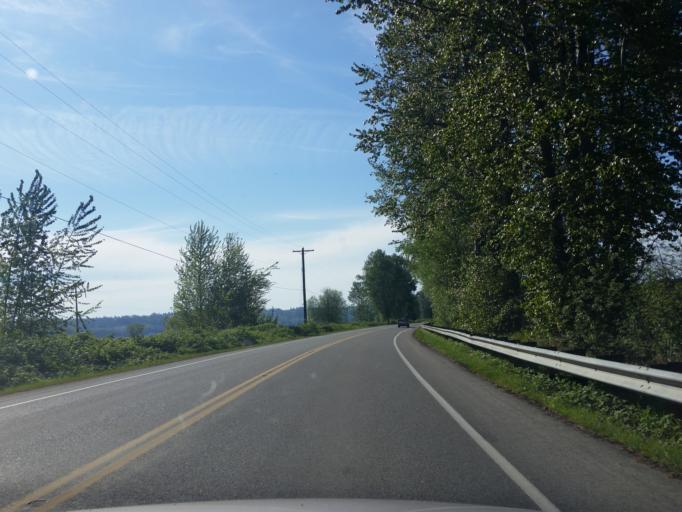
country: US
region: Washington
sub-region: Snohomish County
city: Snohomish
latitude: 47.9117
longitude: -122.1141
